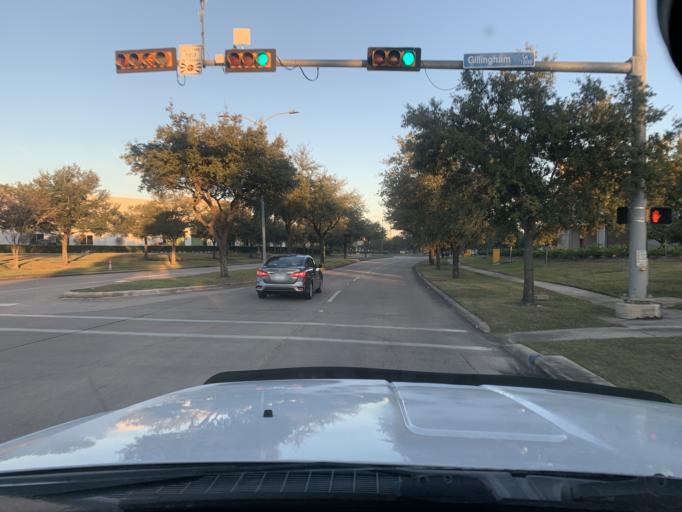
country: US
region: Texas
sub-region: Fort Bend County
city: Meadows Place
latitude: 29.6470
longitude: -95.6121
